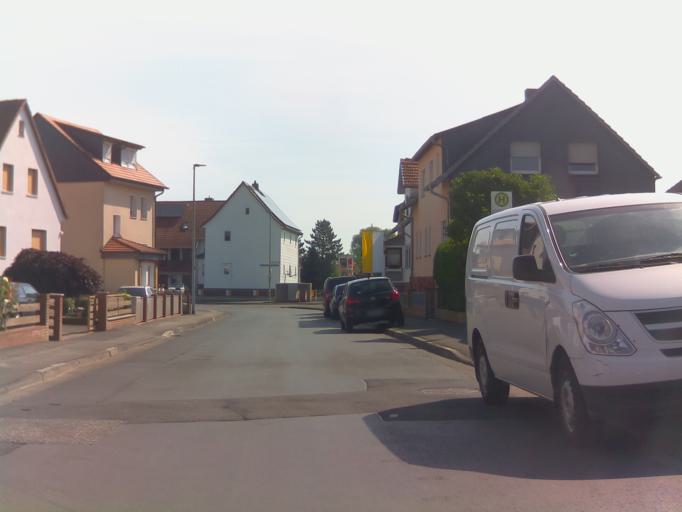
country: DE
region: Hesse
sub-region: Regierungsbezirk Giessen
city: Ebsdorfergrund
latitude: 50.7827
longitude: 8.8292
